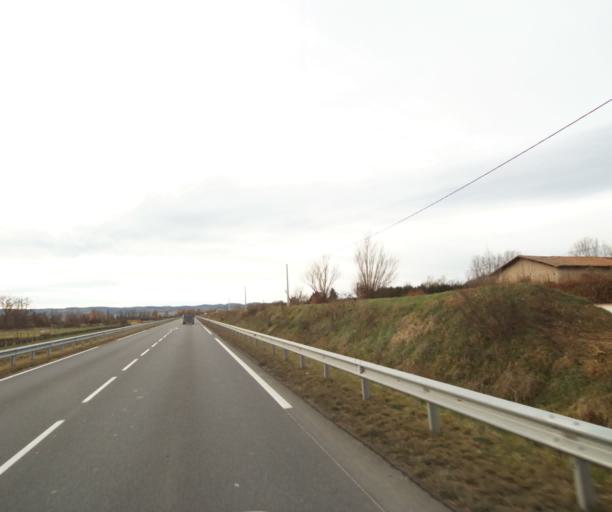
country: FR
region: Rhone-Alpes
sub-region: Departement de la Loire
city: Sury-le-Comtal
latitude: 45.5305
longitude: 4.1975
